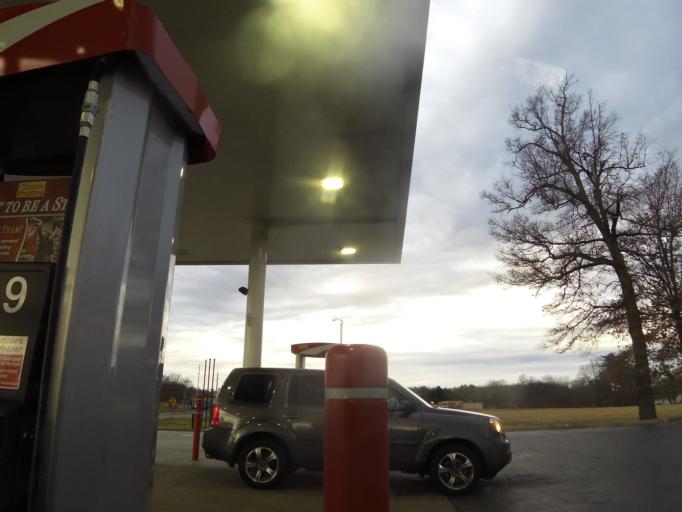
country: US
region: Kentucky
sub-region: McCracken County
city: Hendron
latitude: 37.0545
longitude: -88.6464
